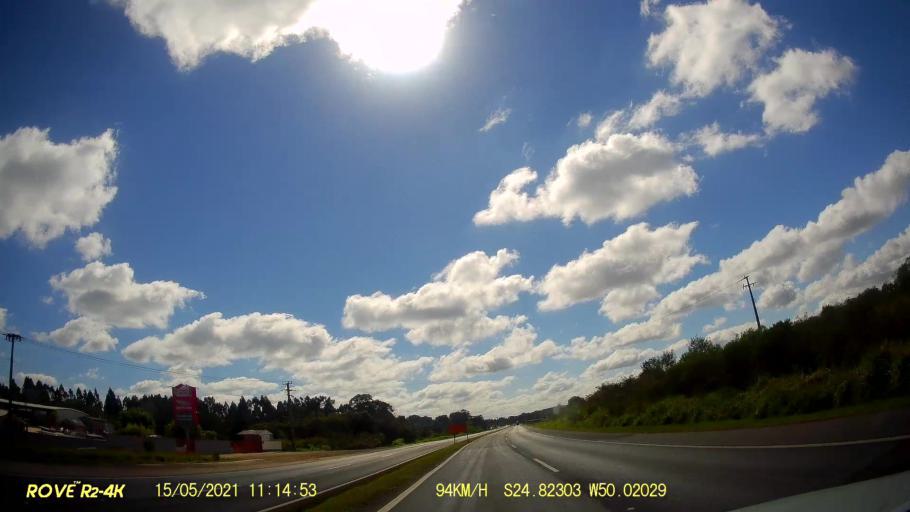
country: BR
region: Parana
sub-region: Castro
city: Castro
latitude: -24.8232
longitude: -50.0203
